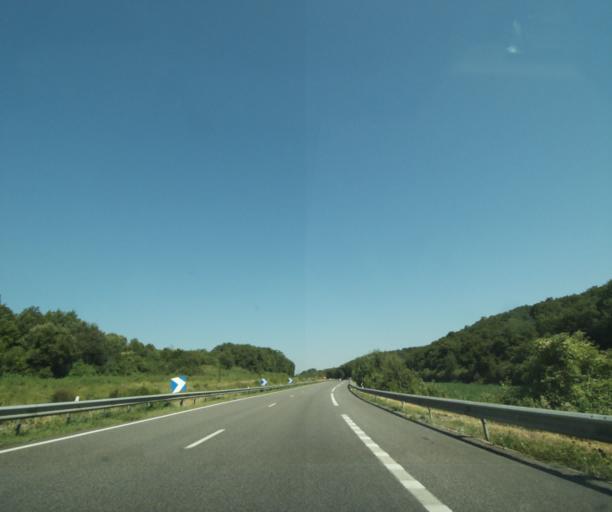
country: FR
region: Lorraine
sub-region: Departement de la Meuse
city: Vacon
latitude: 48.6916
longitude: 5.5521
